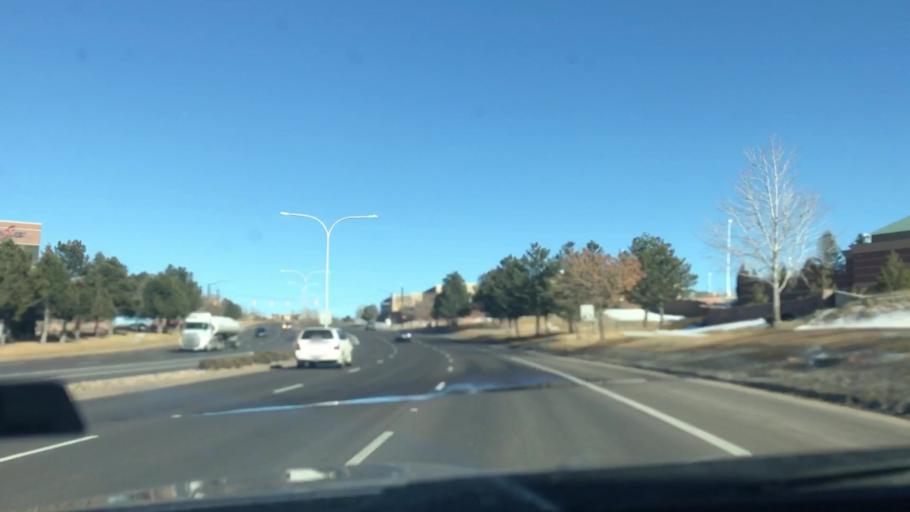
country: US
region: Colorado
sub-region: El Paso County
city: Air Force Academy
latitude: 38.9649
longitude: -104.7912
